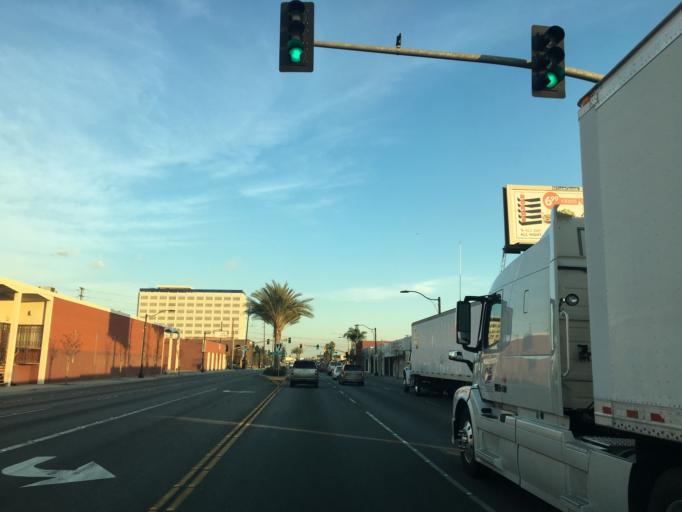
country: US
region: California
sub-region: Los Angeles County
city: Commerce
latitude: 33.9976
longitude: -118.1518
